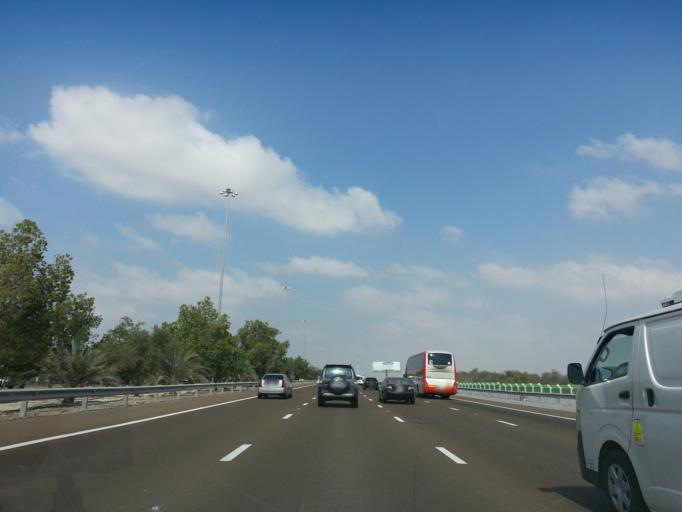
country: AE
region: Dubai
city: Dubai
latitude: 24.7518
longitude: 54.8360
